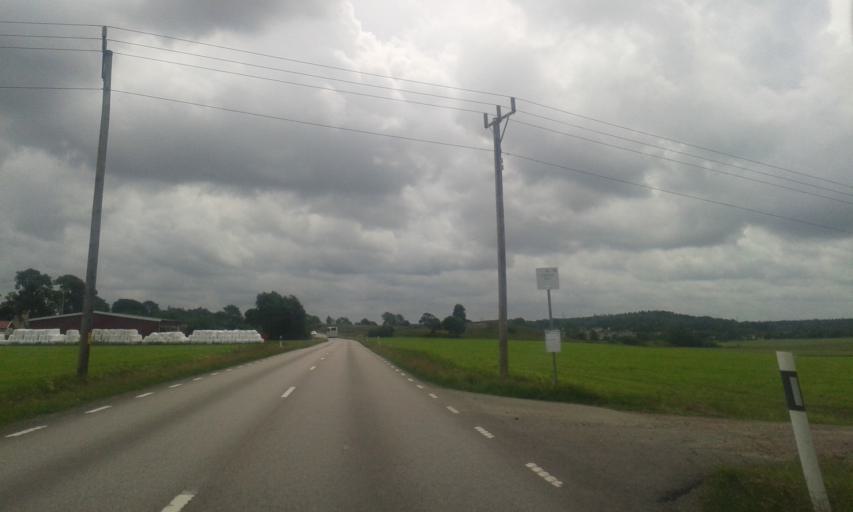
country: SE
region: Vaestra Goetaland
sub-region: Kungalvs Kommun
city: Kode
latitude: 57.8785
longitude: 11.8972
